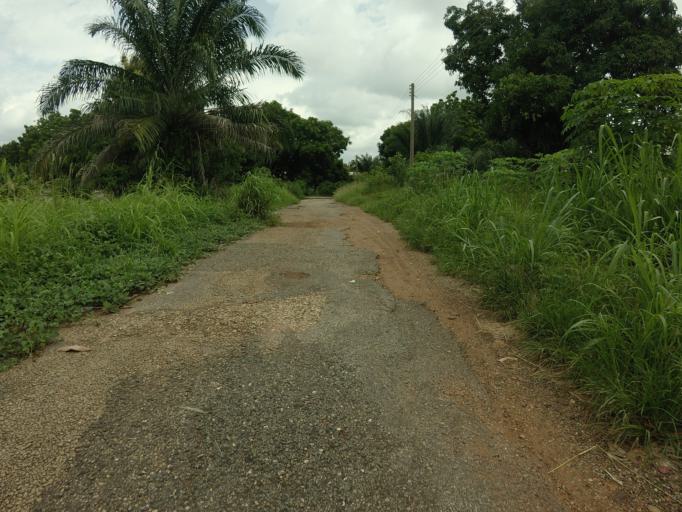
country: GH
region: Volta
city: Ho
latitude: 6.6025
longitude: 0.4591
